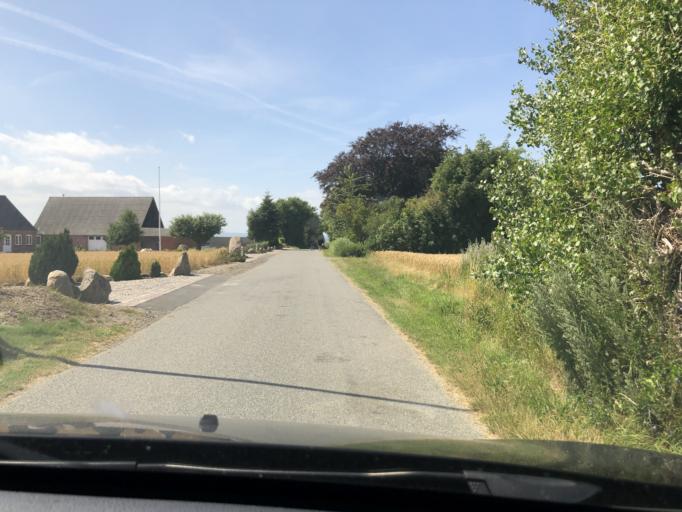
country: DK
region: South Denmark
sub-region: AEro Kommune
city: AEroskobing
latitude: 54.8947
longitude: 10.2924
